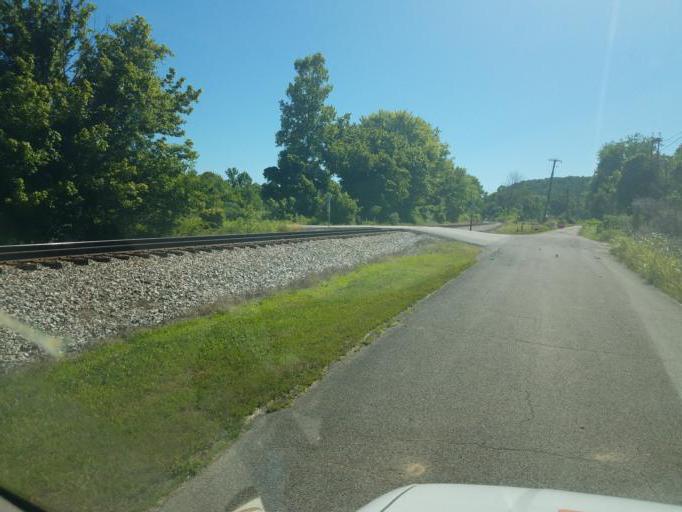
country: US
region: West Virginia
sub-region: Cabell County
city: Lesage
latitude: 38.5846
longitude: -82.2169
